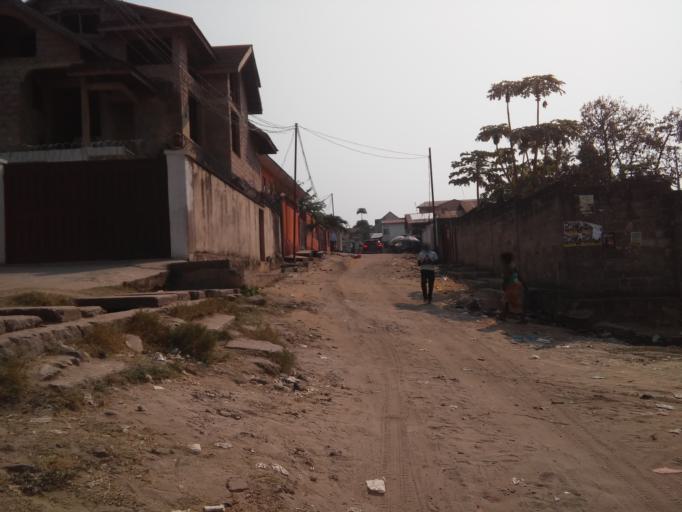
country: CD
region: Kinshasa
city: Kinshasa
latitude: -4.3433
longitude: 15.2653
